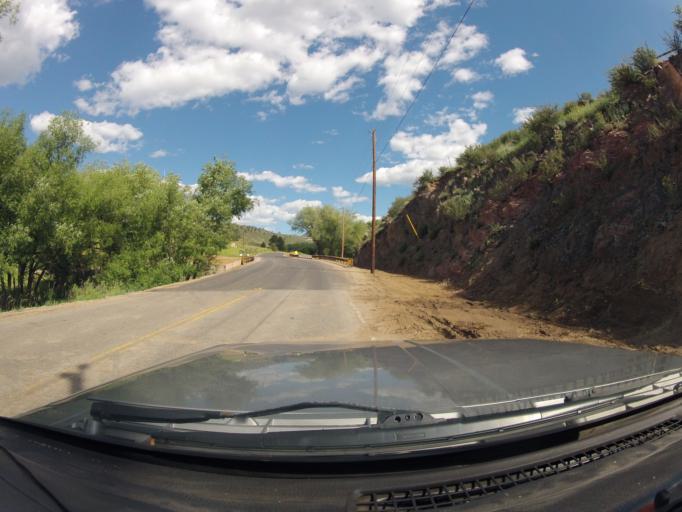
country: US
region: Colorado
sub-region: Larimer County
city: Laporte
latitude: 40.5392
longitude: -105.2779
